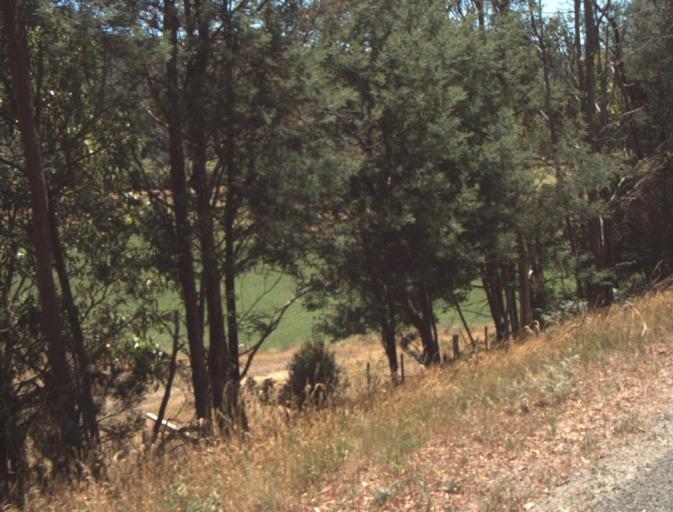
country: AU
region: Tasmania
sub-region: Dorset
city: Scottsdale
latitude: -41.3199
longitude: 147.3636
